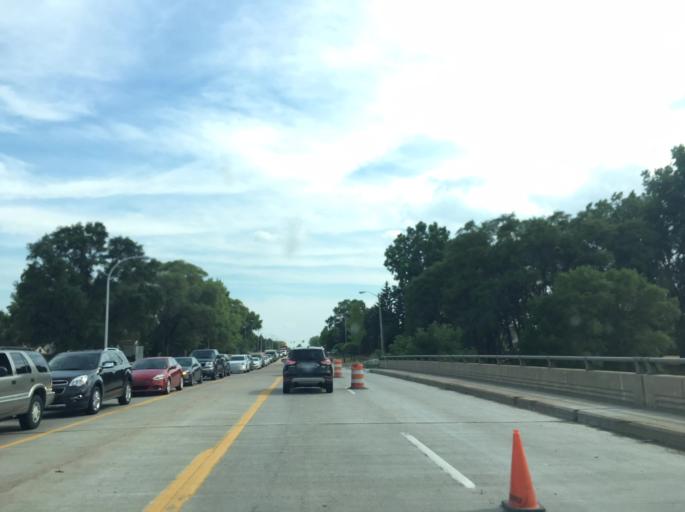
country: US
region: Michigan
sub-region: Macomb County
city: Fraser
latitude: 42.5498
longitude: -82.9897
